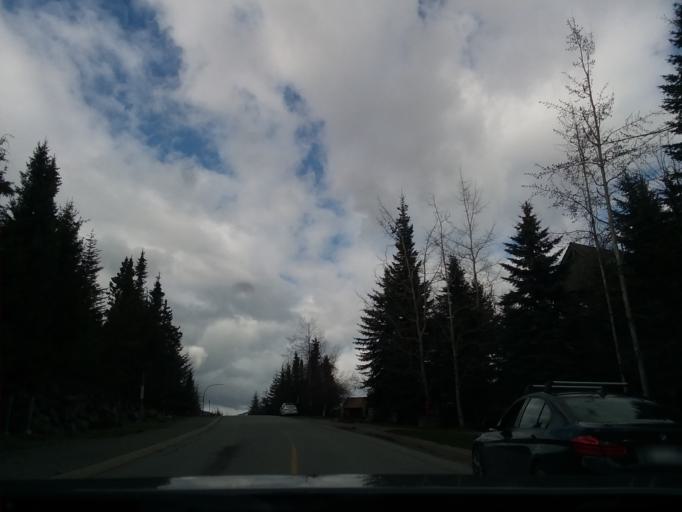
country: CA
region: British Columbia
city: Whistler
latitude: 50.1125
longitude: -122.9704
